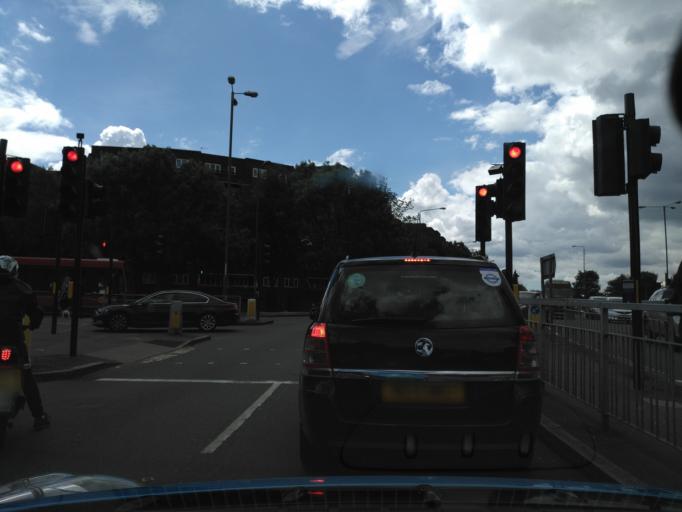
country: GB
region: England
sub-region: Greater London
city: Woolwich
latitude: 51.4827
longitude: 0.0621
